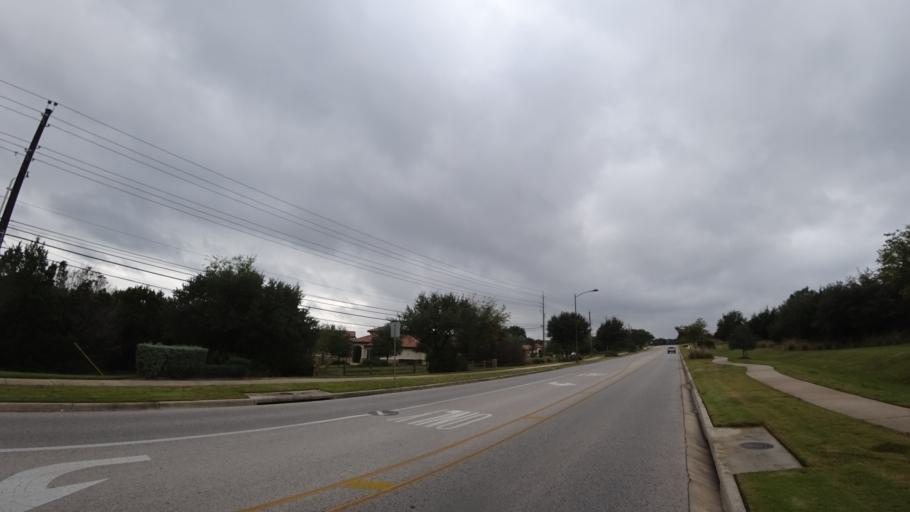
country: US
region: Texas
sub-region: Travis County
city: Bee Cave
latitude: 30.3546
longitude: -97.9104
